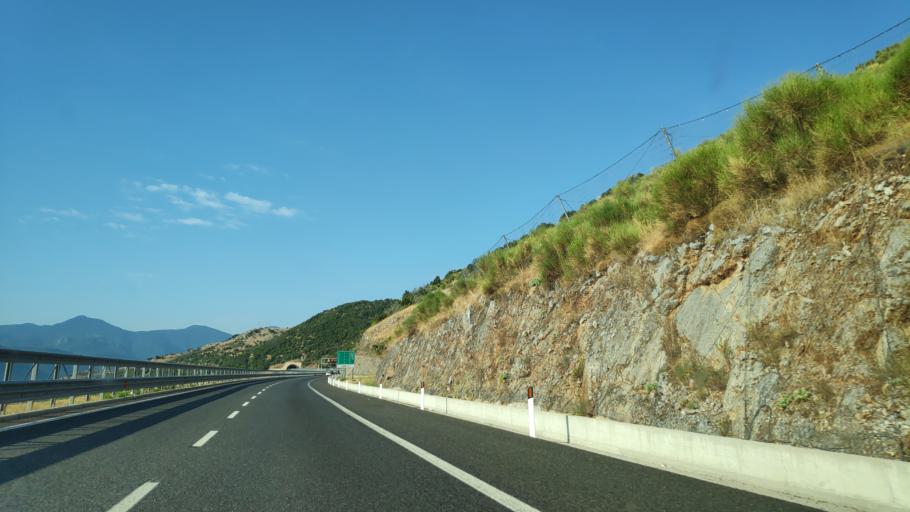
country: IT
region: Calabria
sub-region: Provincia di Cosenza
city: Morano Calabro
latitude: 39.8833
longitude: 16.1328
